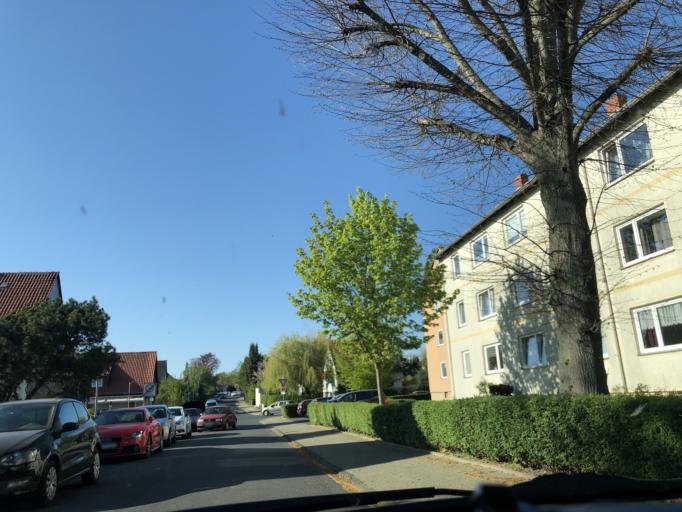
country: DE
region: Lower Saxony
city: Wolfenbuettel
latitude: 52.1700
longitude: 10.5618
